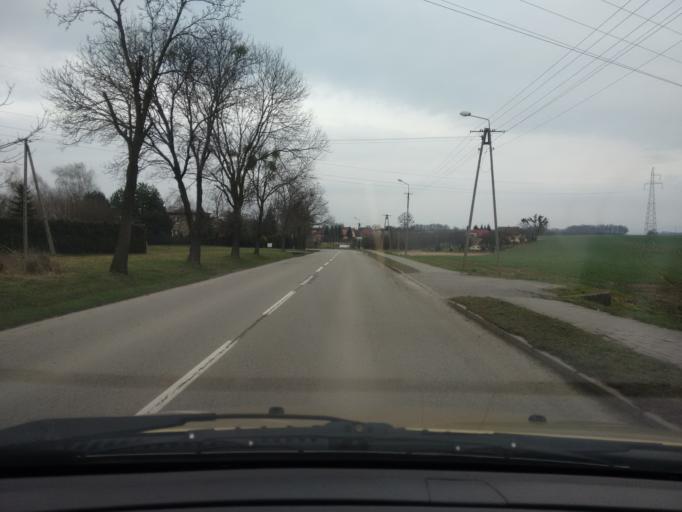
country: PL
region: Silesian Voivodeship
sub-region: Powiat pszczynski
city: Pawlowice
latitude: 49.9612
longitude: 18.7280
